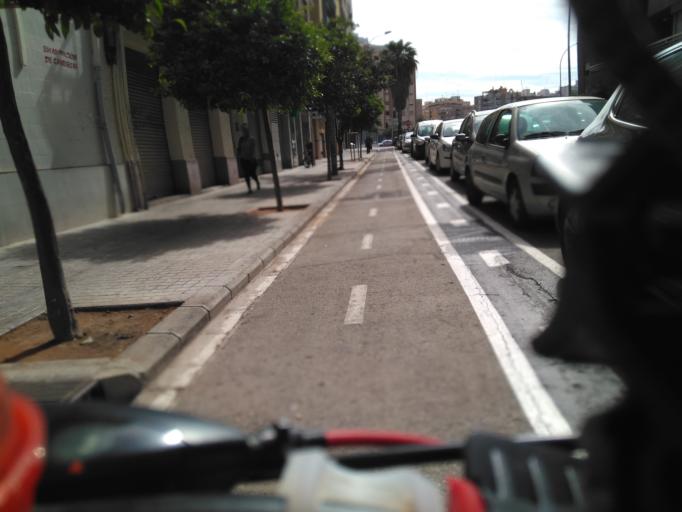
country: ES
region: Valencia
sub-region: Provincia de Valencia
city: Valencia
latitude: 39.4863
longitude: -0.3900
